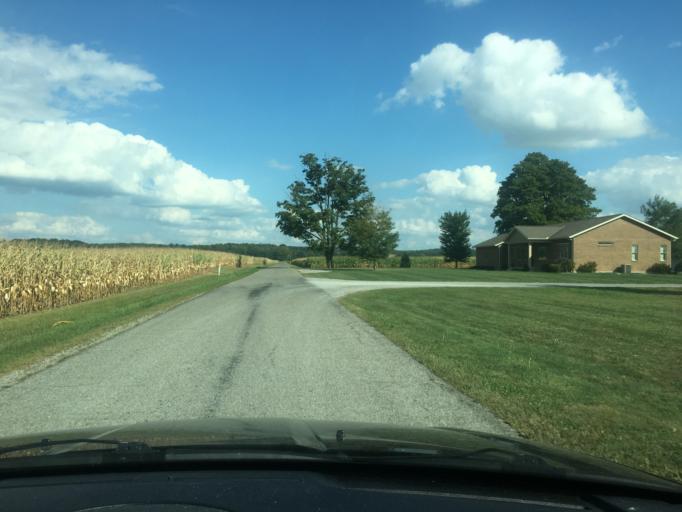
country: US
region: Ohio
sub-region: Logan County
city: West Liberty
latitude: 40.2454
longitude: -83.7411
